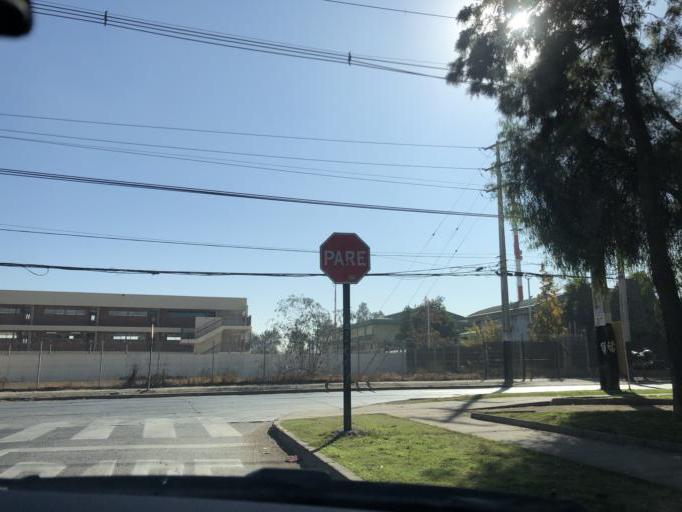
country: CL
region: Santiago Metropolitan
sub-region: Provincia de Cordillera
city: Puente Alto
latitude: -33.6169
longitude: -70.6111
